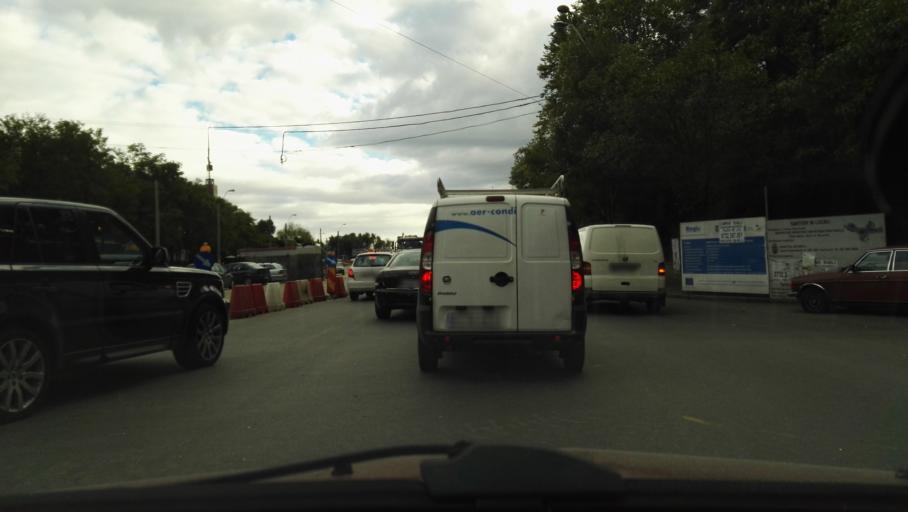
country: RO
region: Bucuresti
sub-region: Municipiul Bucuresti
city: Bucharest
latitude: 44.3962
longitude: 26.1207
